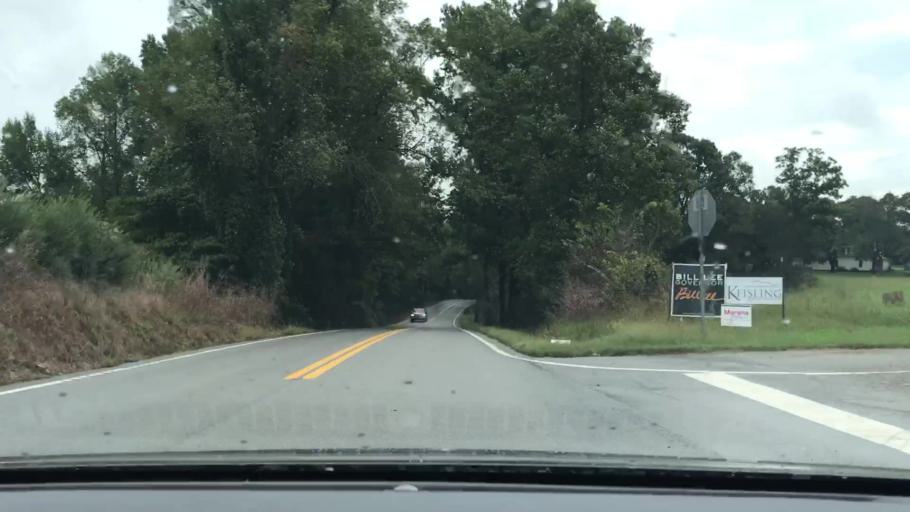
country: US
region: Tennessee
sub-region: Macon County
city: Red Boiling Springs
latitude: 36.5609
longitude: -85.8000
